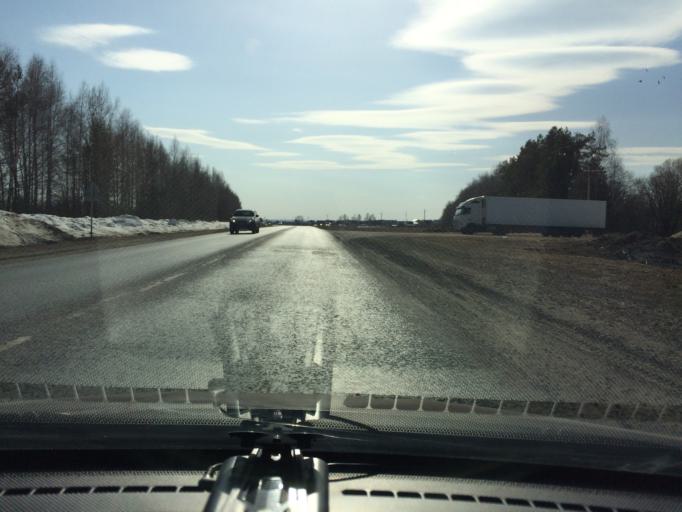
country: RU
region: Mariy-El
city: Yoshkar-Ola
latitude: 56.7189
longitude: 48.1014
